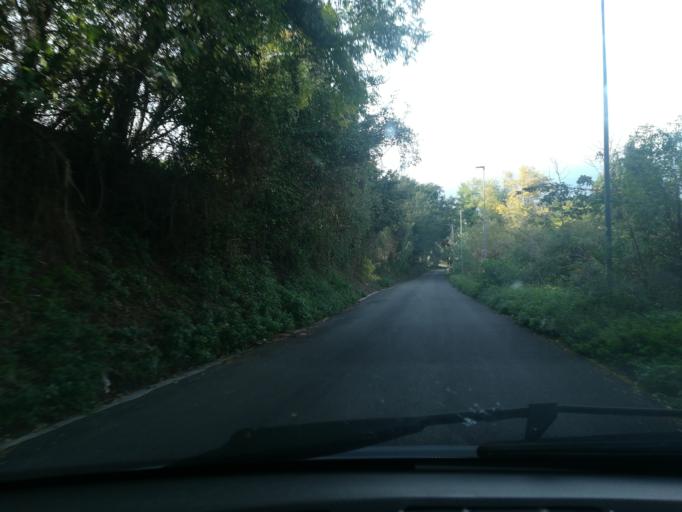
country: IT
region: The Marches
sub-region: Provincia di Macerata
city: Macerata
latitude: 43.3048
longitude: 13.4529
